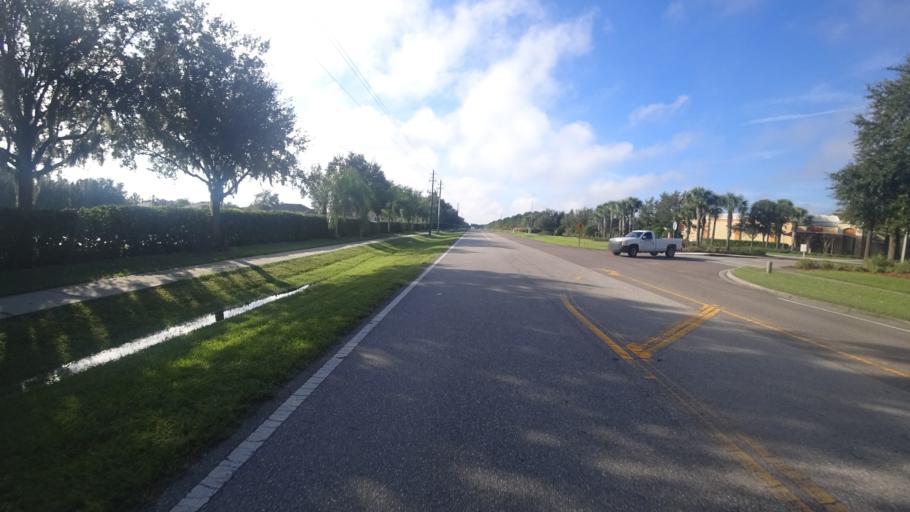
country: US
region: Florida
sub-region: Manatee County
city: Ellenton
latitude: 27.5575
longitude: -82.4459
